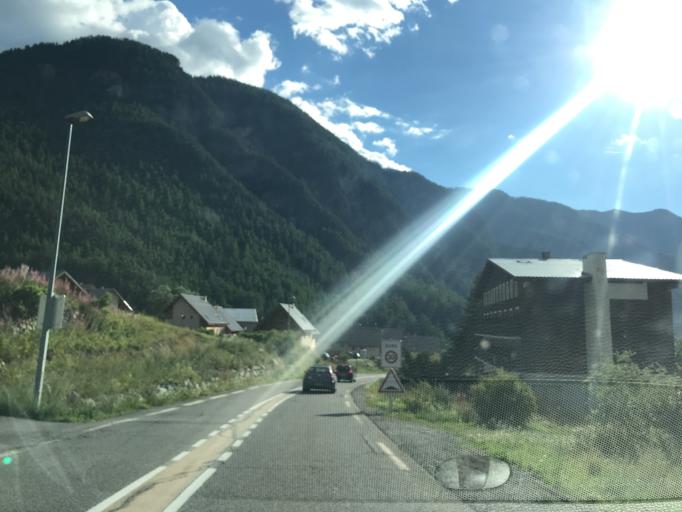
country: IT
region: Piedmont
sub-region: Provincia di Torino
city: Claviere
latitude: 44.8689
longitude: 6.7233
